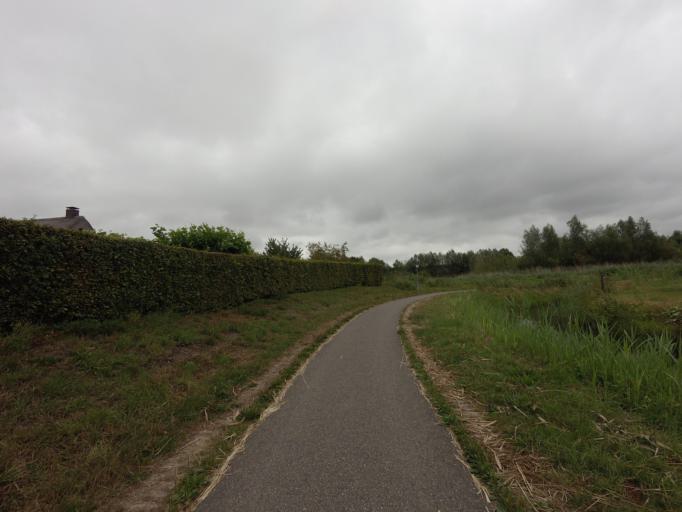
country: NL
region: Gelderland
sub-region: Gemeente Overbetuwe
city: Driel
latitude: 51.9588
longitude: 5.8310
